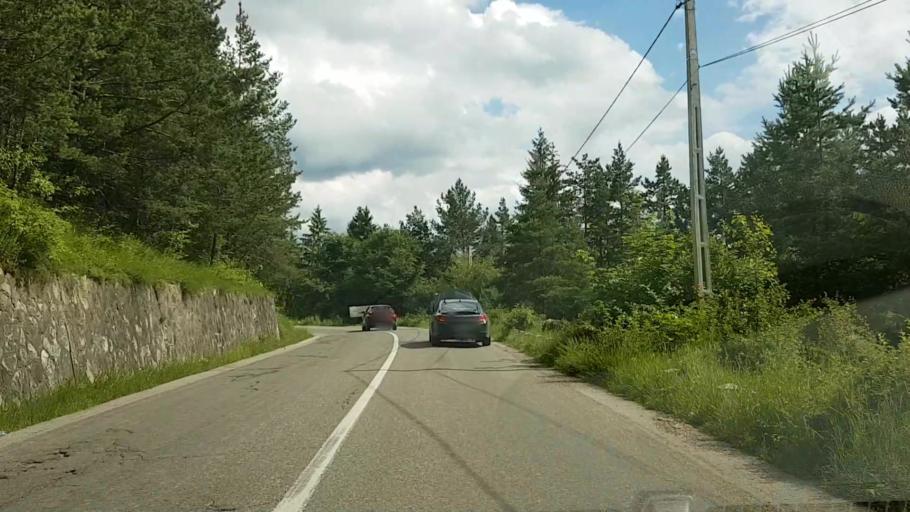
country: RO
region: Neamt
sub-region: Comuna Hangu
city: Hangu
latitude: 47.0108
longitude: 26.0846
